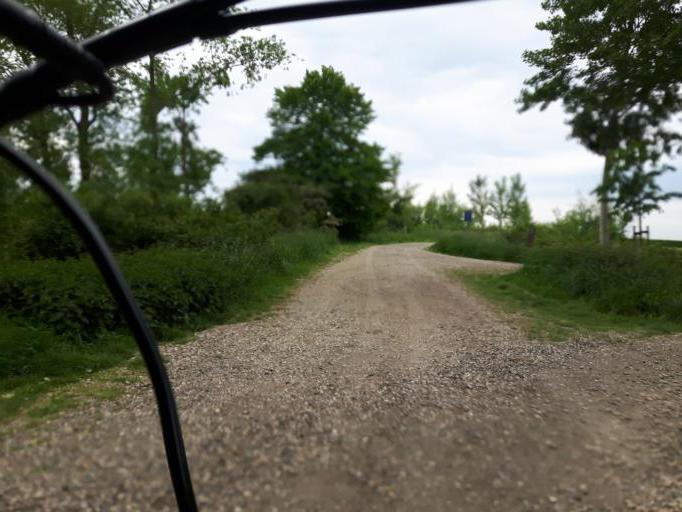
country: NL
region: Zeeland
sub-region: Gemeente Goes
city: Goes
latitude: 51.4482
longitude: 3.8326
